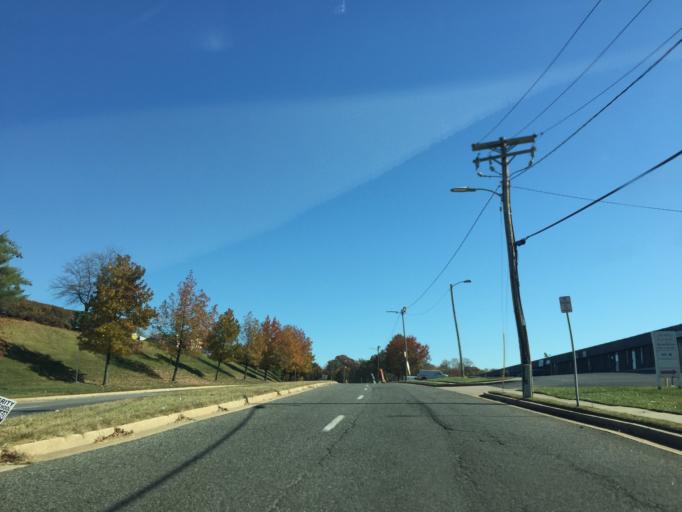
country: US
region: Maryland
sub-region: Baltimore County
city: Lansdowne
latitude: 39.2530
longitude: -76.6676
